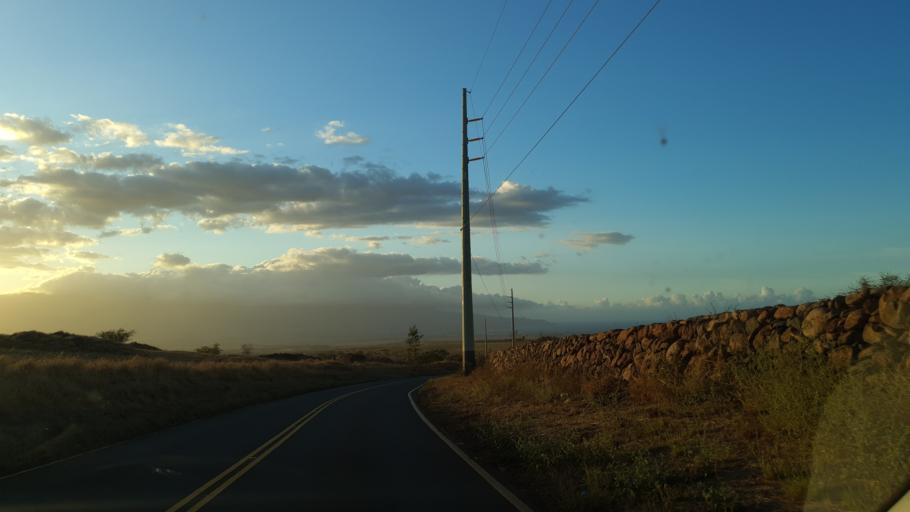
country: US
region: Hawaii
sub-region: Maui County
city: Pukalani
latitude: 20.8004
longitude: -156.3739
